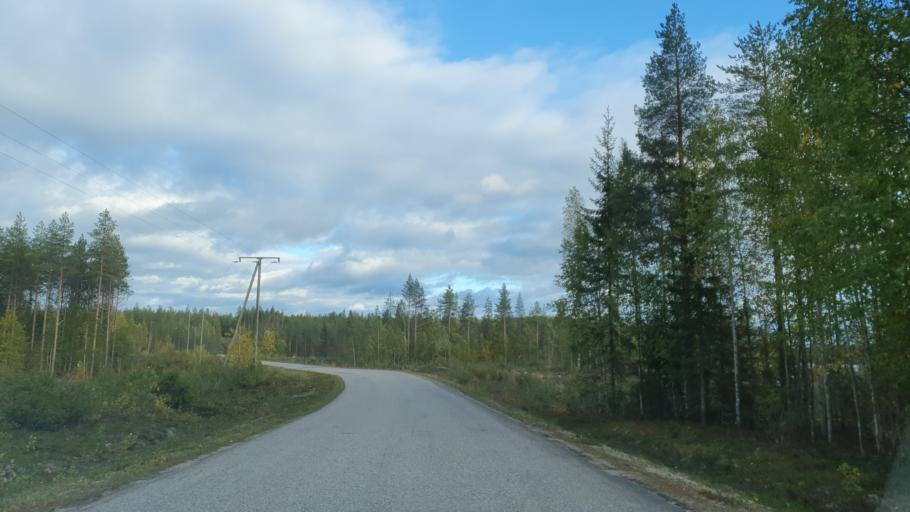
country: FI
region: Kainuu
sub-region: Kehys-Kainuu
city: Kuhmo
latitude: 63.9274
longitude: 30.0036
